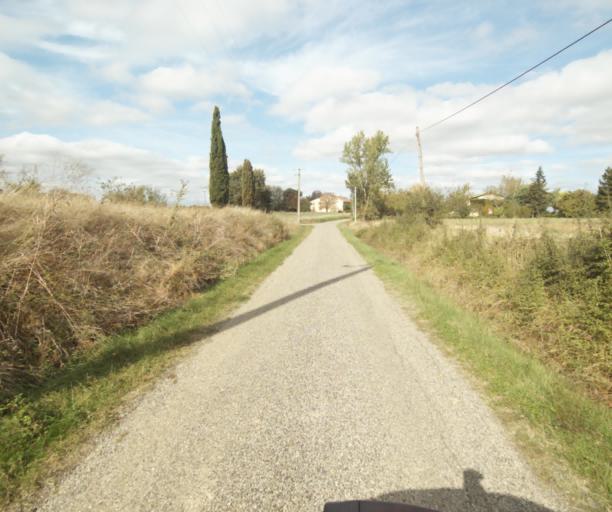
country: FR
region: Midi-Pyrenees
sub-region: Departement du Tarn-et-Garonne
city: Saint-Porquier
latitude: 43.9483
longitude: 1.1502
